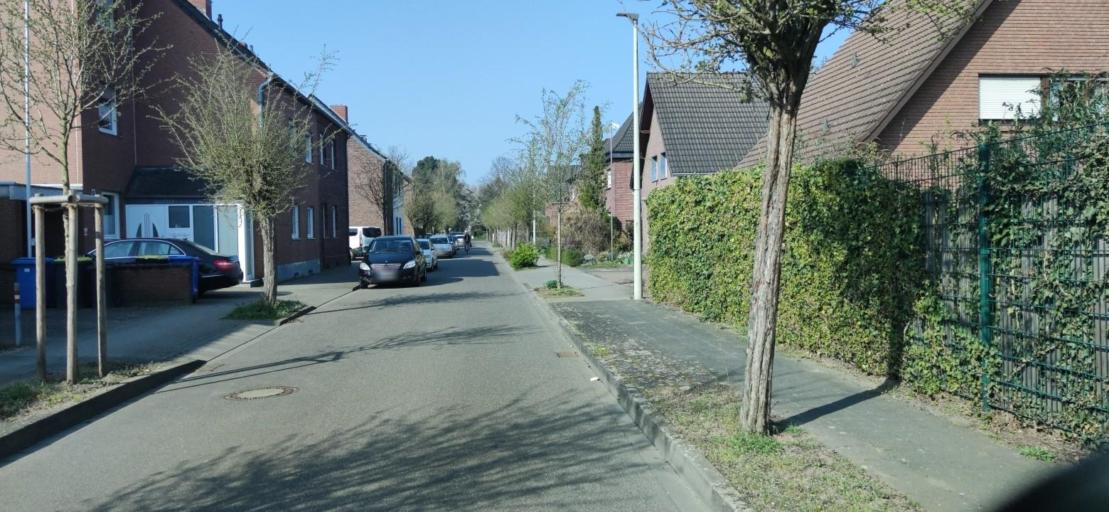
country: DE
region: North Rhine-Westphalia
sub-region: Regierungsbezirk Dusseldorf
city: Kaarst
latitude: 51.2004
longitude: 6.6089
